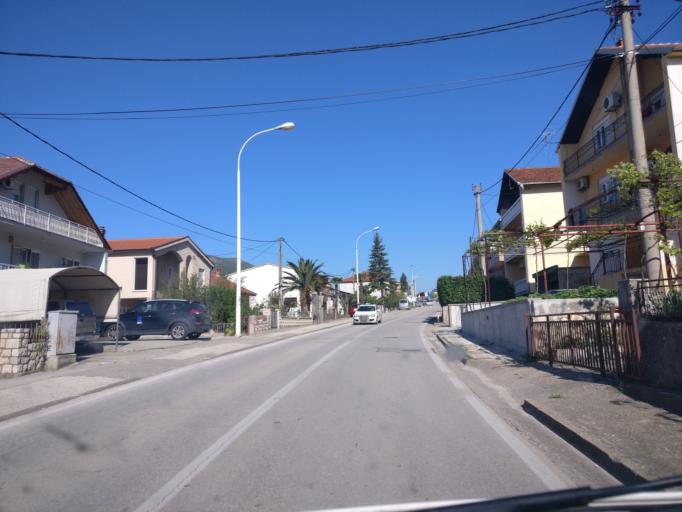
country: BA
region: Federation of Bosnia and Herzegovina
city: Capljina
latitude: 43.1196
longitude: 17.6886
